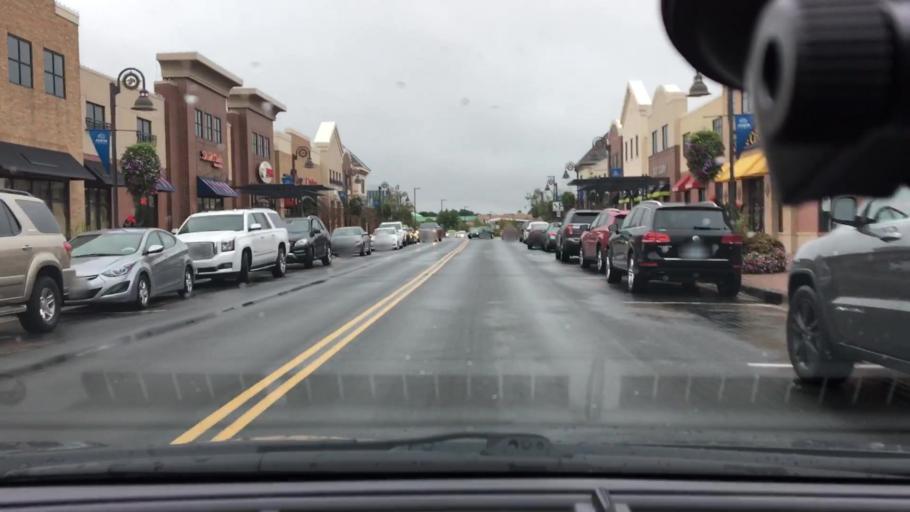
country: US
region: Minnesota
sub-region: Hennepin County
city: Maple Grove
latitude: 45.0973
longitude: -93.4417
